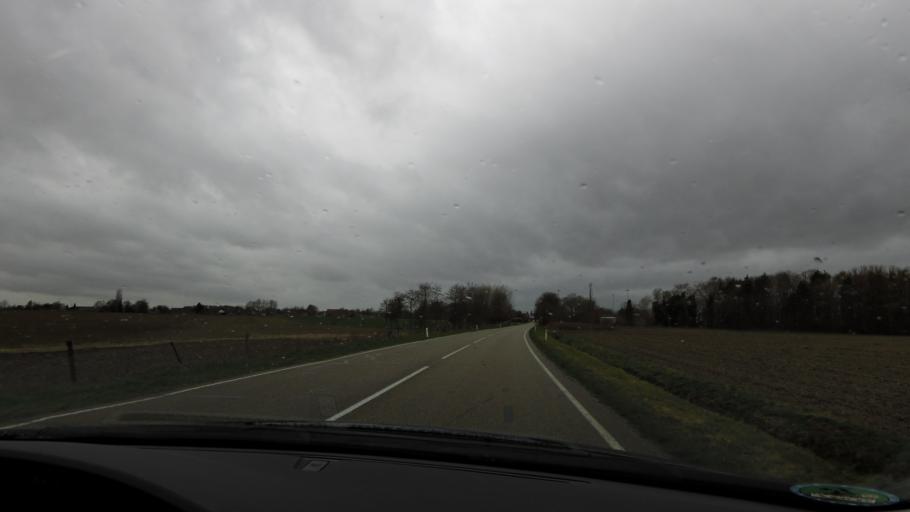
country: NL
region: Limburg
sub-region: Gemeente Beek
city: Beek
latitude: 50.9077
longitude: 5.7954
